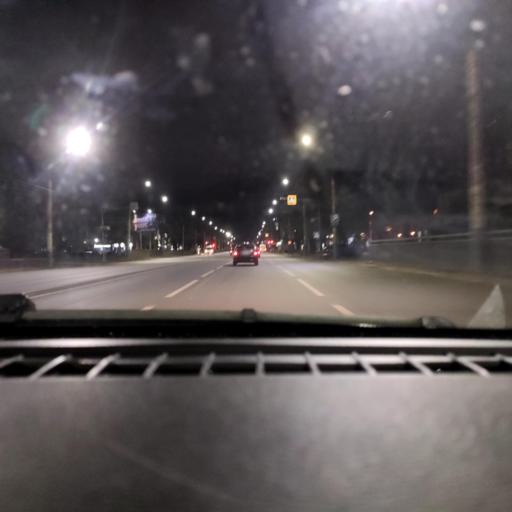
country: RU
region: Voronezj
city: Voronezh
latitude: 51.6917
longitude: 39.2680
